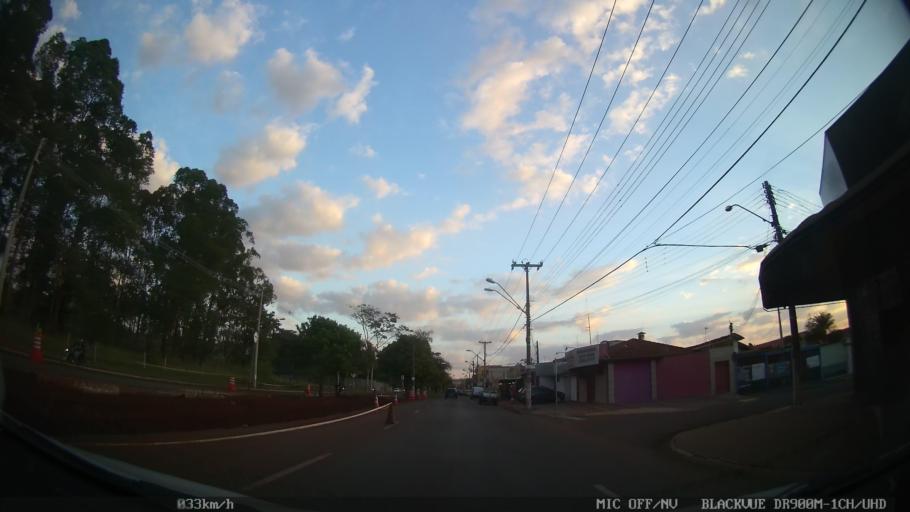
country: BR
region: Sao Paulo
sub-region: Ribeirao Preto
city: Ribeirao Preto
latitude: -21.1586
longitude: -47.7859
